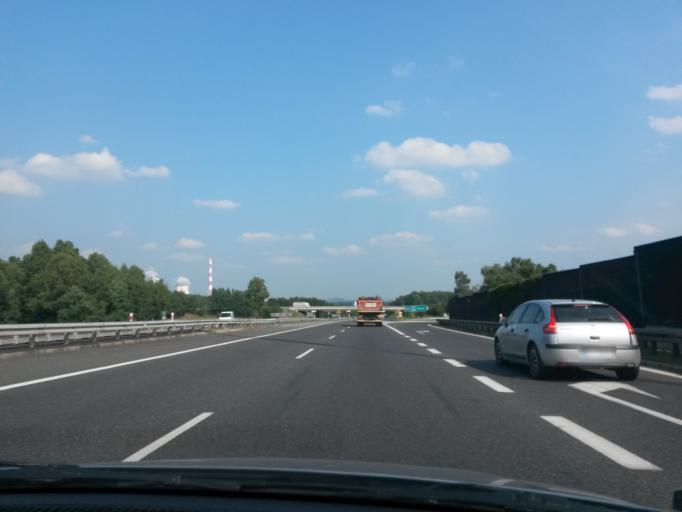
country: PL
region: Silesian Voivodeship
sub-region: Myslowice
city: Myslowice
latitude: 50.2088
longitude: 19.1615
